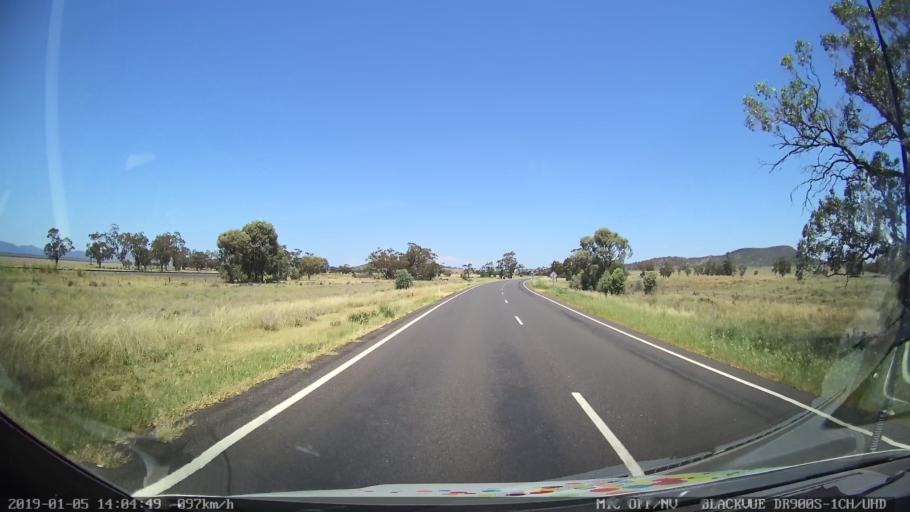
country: AU
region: New South Wales
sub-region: Gunnedah
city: Gunnedah
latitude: -31.2038
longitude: 150.3685
